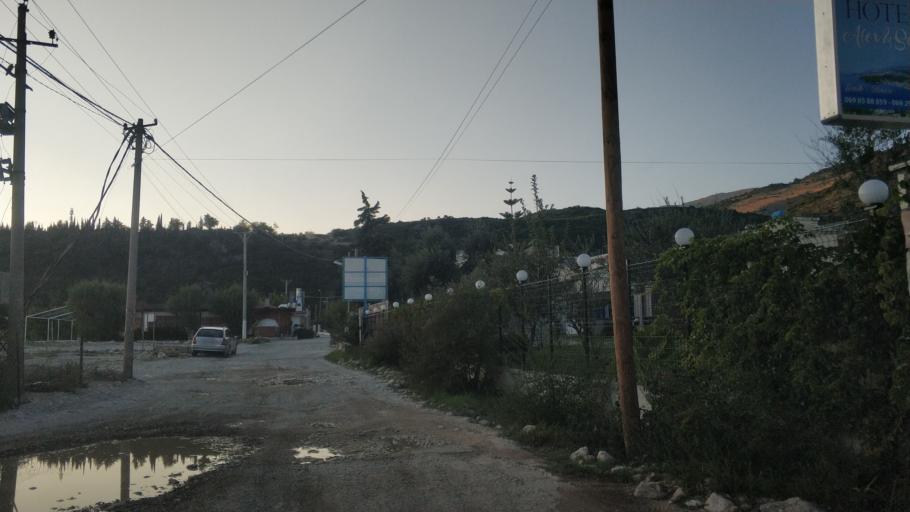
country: AL
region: Vlore
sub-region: Rrethi i Vlores
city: Himare
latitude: 40.1094
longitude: 19.7240
